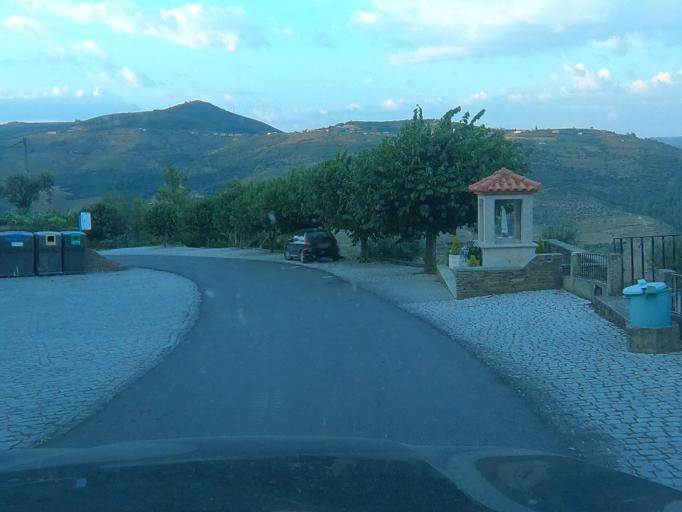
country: PT
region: Vila Real
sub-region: Sabrosa
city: Vilela
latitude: 41.1986
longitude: -7.5740
